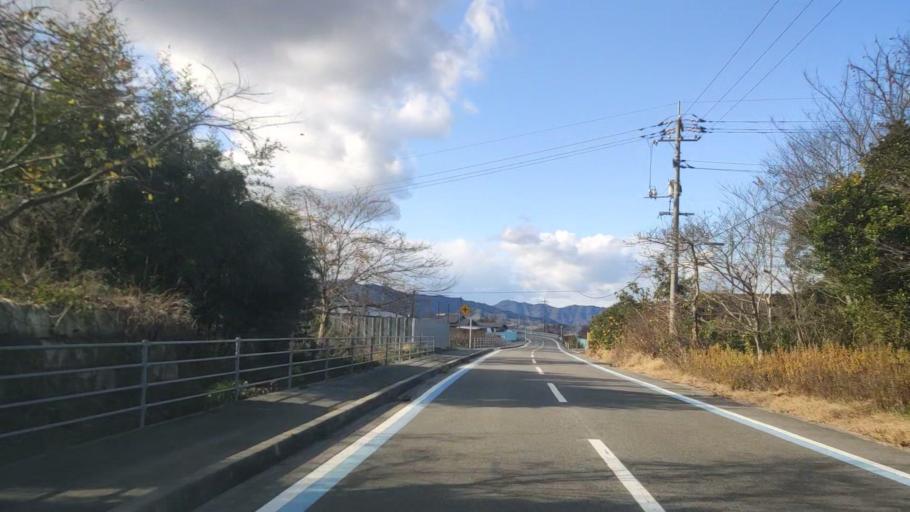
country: JP
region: Hiroshima
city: Innoshima
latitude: 34.2307
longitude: 133.0886
